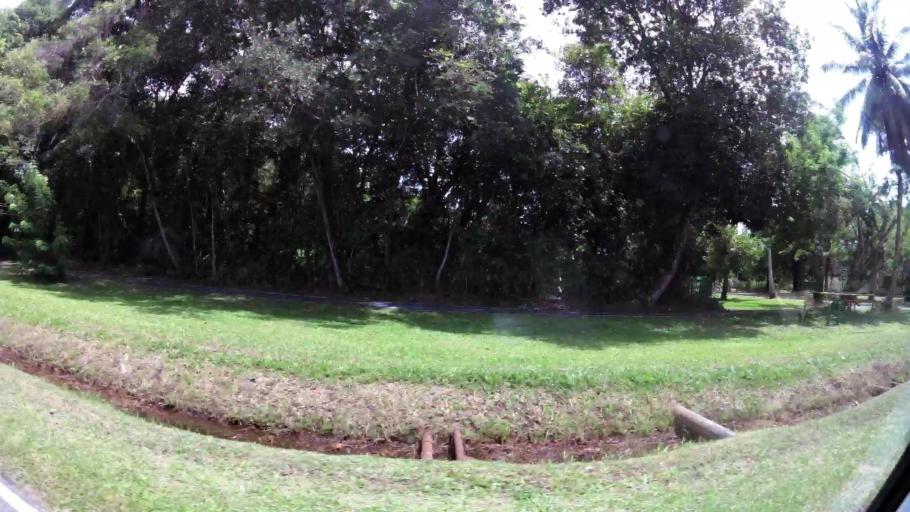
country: BN
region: Belait
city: Seria
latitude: 4.6046
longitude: 114.2849
